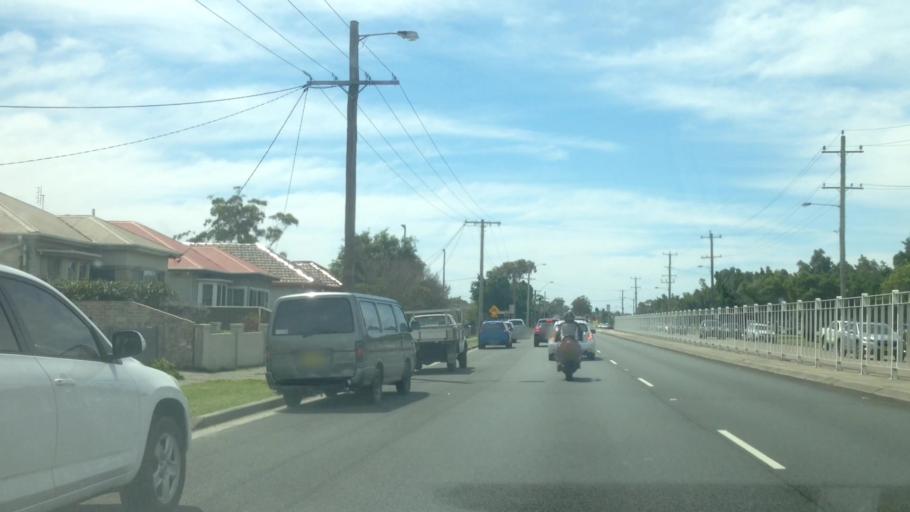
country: AU
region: New South Wales
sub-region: Newcastle
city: Broadmeadow
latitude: -32.9214
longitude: 151.7235
